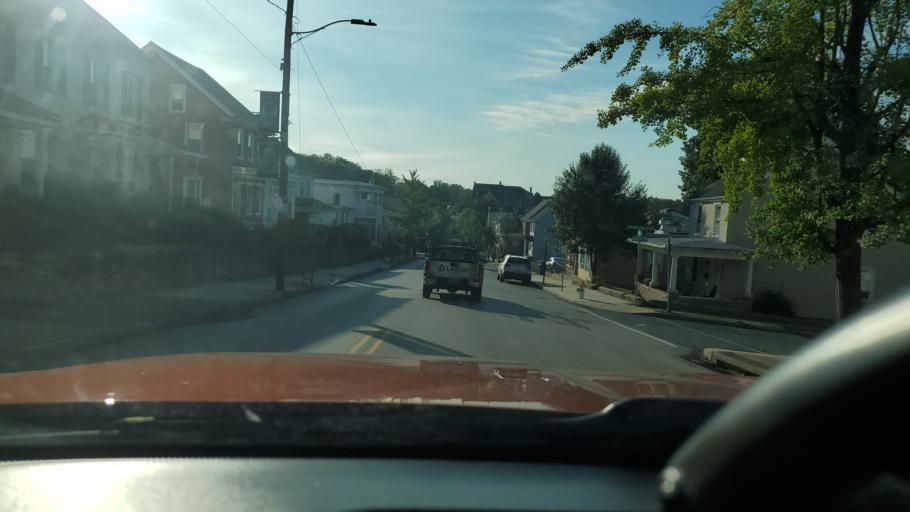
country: US
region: Pennsylvania
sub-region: Montgomery County
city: Souderton
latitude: 40.3119
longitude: -75.3251
